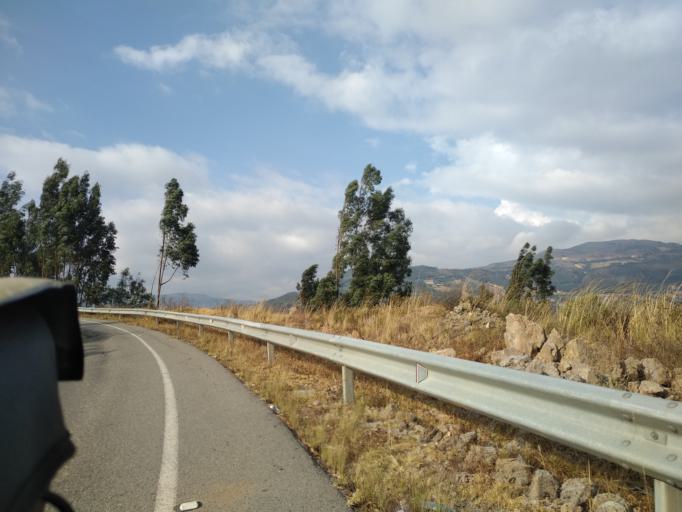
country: PE
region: La Libertad
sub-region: Provincia de Otuzco
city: Agallpampa
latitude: -7.9888
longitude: -78.5339
